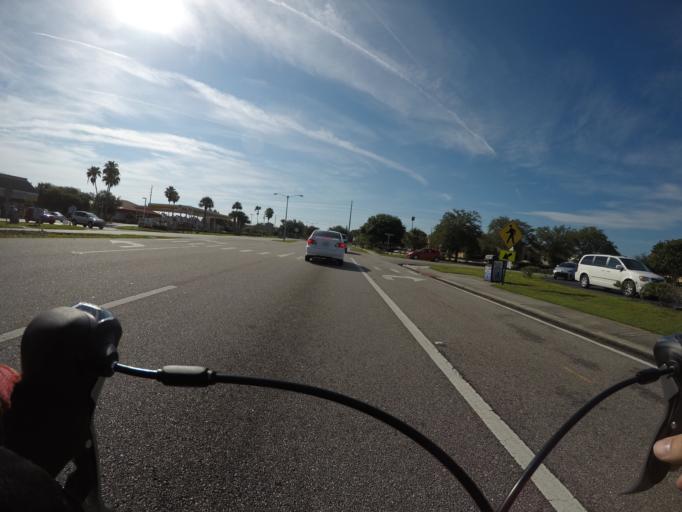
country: US
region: Florida
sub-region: Osceola County
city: Buenaventura Lakes
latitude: 28.3204
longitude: -81.3406
